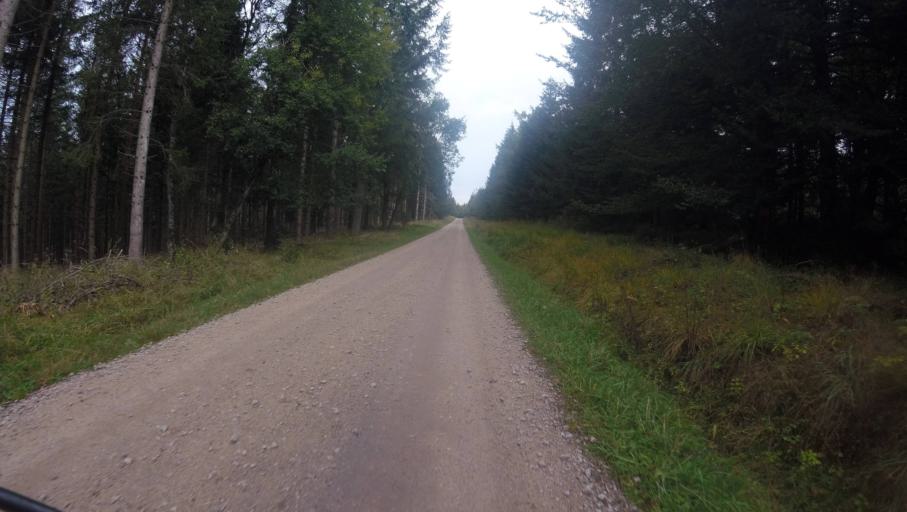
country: DE
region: Baden-Wuerttemberg
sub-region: Karlsruhe Region
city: Loffenau
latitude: 48.7310
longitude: 8.4300
